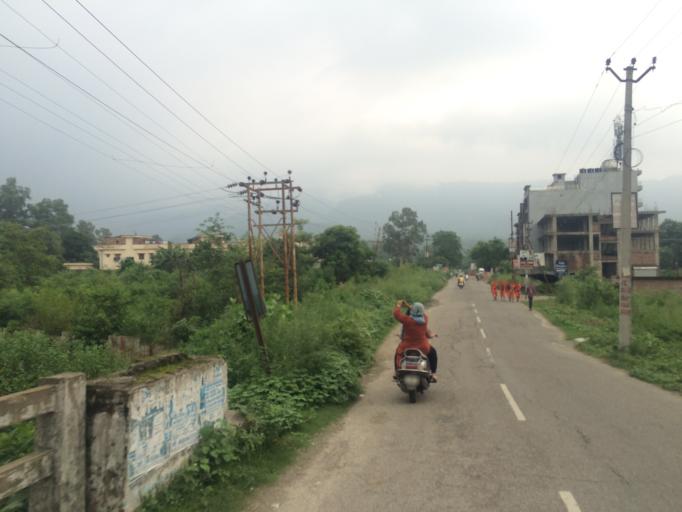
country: IN
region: Uttarakhand
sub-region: Dehradun
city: Birbhaddar
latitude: 30.0728
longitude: 78.2794
